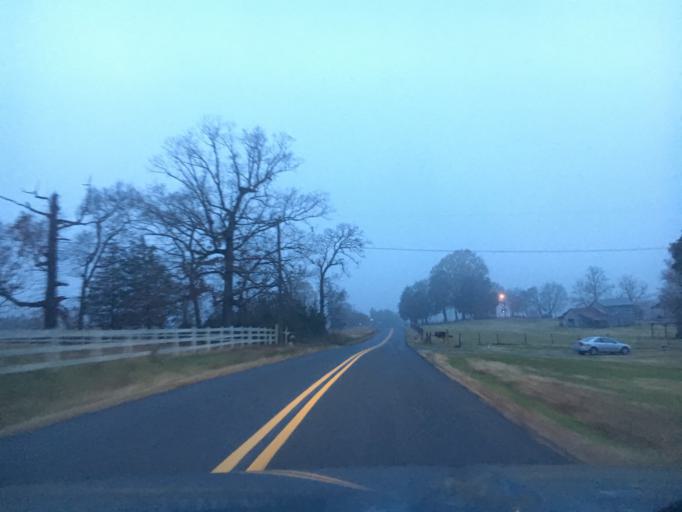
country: US
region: Virginia
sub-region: Halifax County
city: Mountain Road
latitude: 36.6799
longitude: -79.0273
